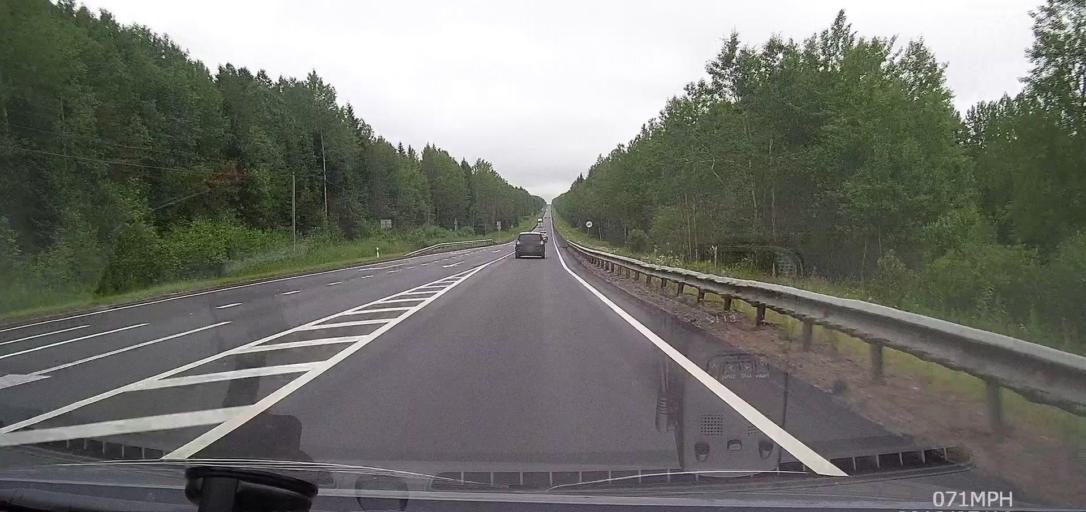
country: RU
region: Leningrad
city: Pasha
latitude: 60.2794
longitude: 32.8096
